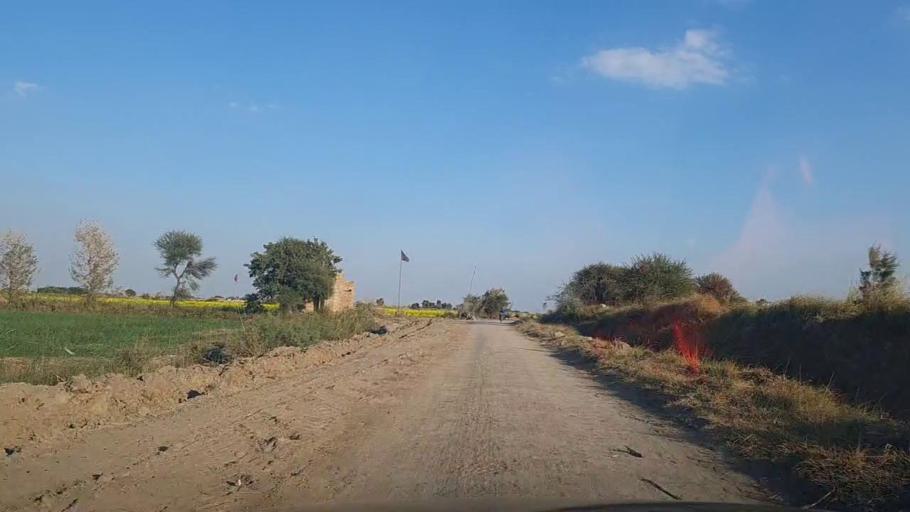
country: PK
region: Sindh
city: Jhol
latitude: 25.9209
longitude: 69.0373
